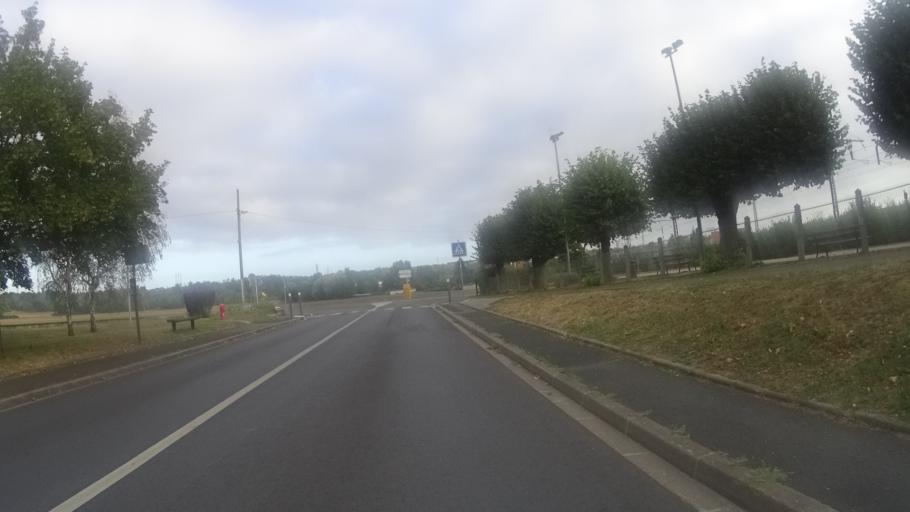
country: FR
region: Ile-de-France
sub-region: Departement de l'Essonne
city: Villabe
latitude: 48.5938
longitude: 2.4598
